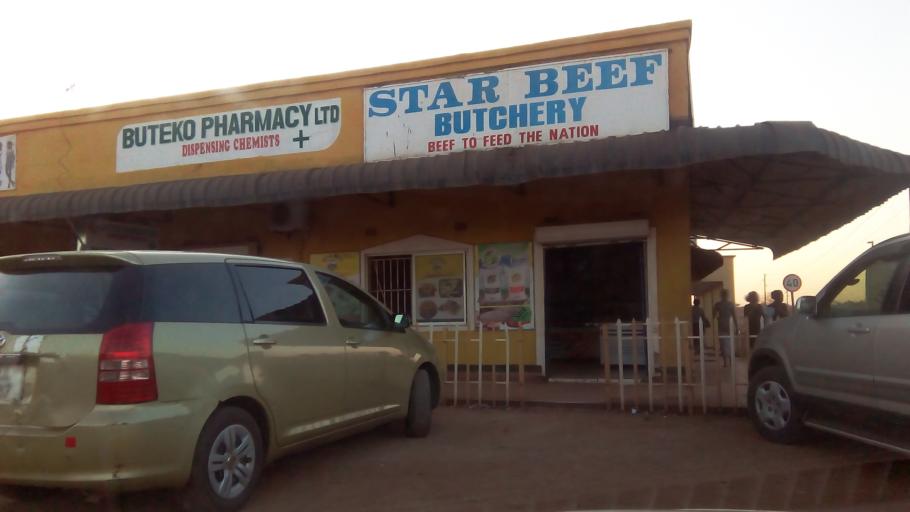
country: ZM
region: Lusaka
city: Lusaka
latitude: -15.4502
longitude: 28.3475
